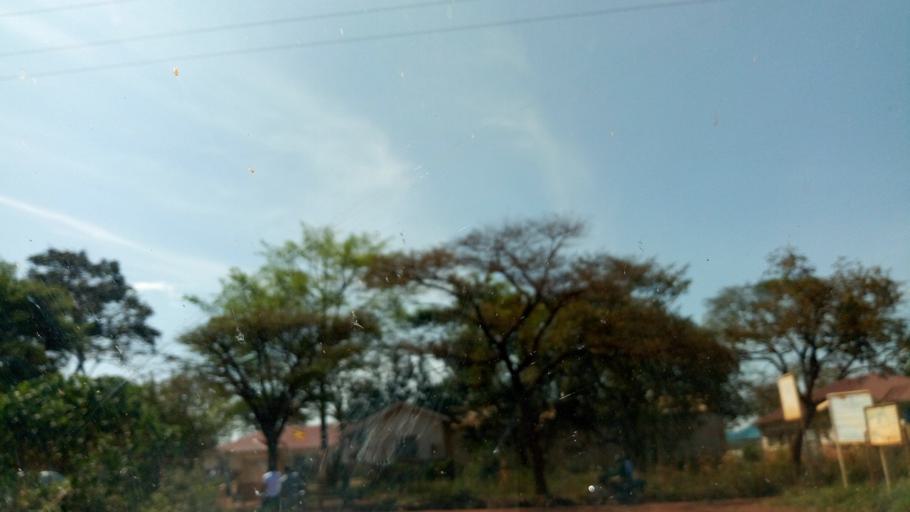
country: UG
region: Western Region
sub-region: Kiryandongo District
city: Kiryandongo
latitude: 1.9444
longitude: 32.1571
